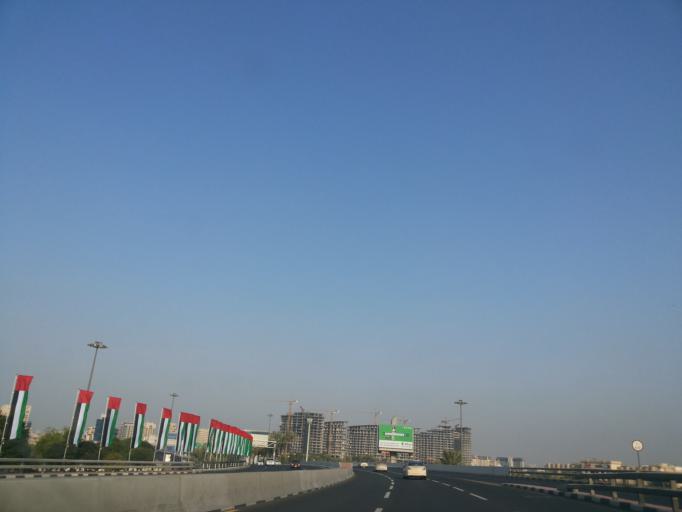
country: AE
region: Ash Shariqah
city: Sharjah
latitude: 25.2487
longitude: 55.3171
